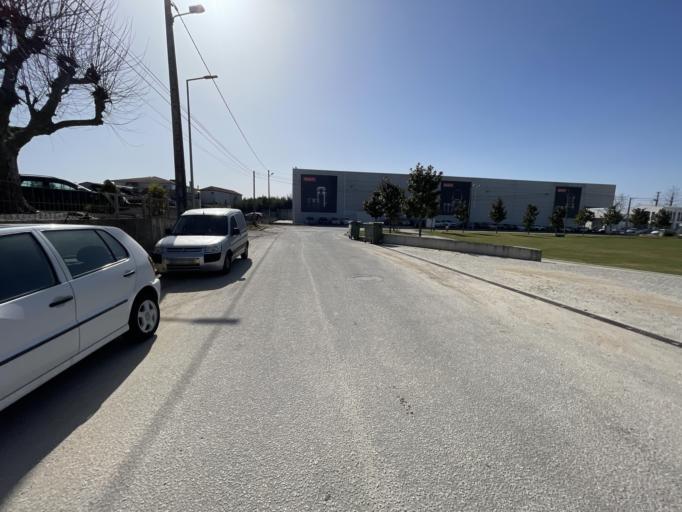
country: PT
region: Viseu
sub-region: Concelho de Tondela
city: Tondela
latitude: 40.4827
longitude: -8.0918
